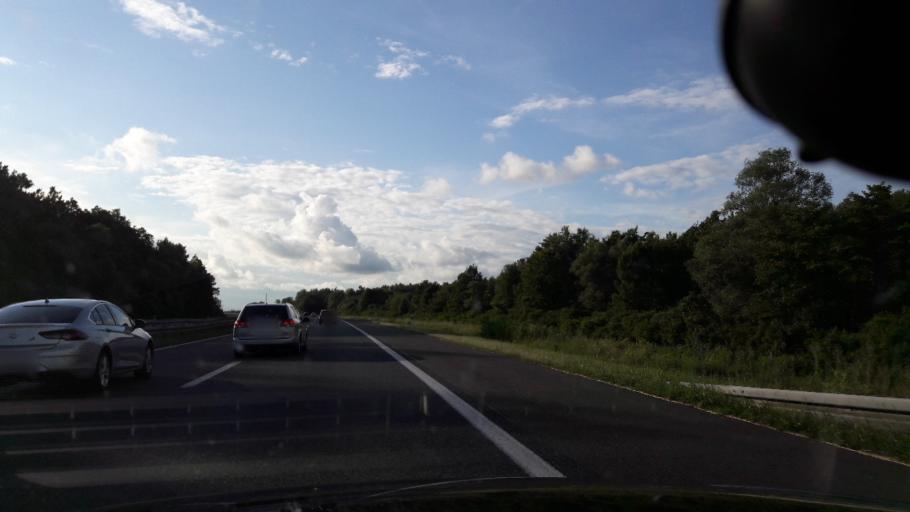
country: HR
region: Zagrebacka
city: Novoselec
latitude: 45.6076
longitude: 16.5486
